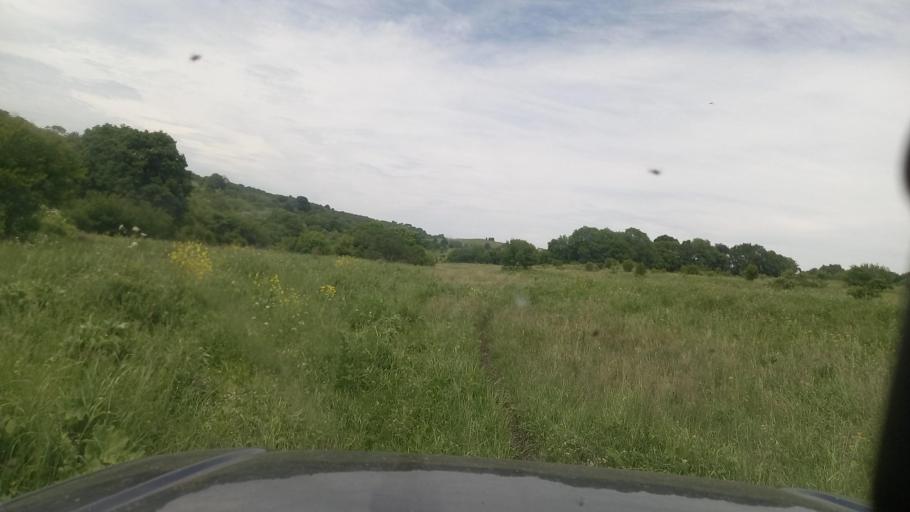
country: RU
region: Karachayevo-Cherkesiya
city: Pregradnaya
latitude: 44.0930
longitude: 41.1738
